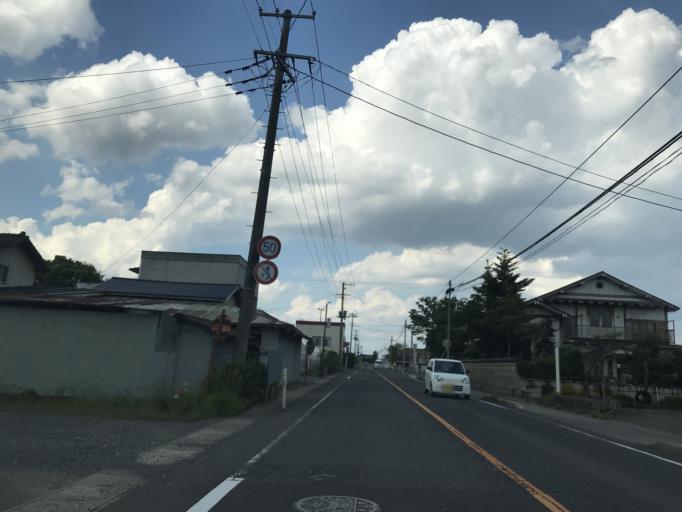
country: JP
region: Miyagi
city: Wakuya
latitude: 38.6117
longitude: 141.1768
